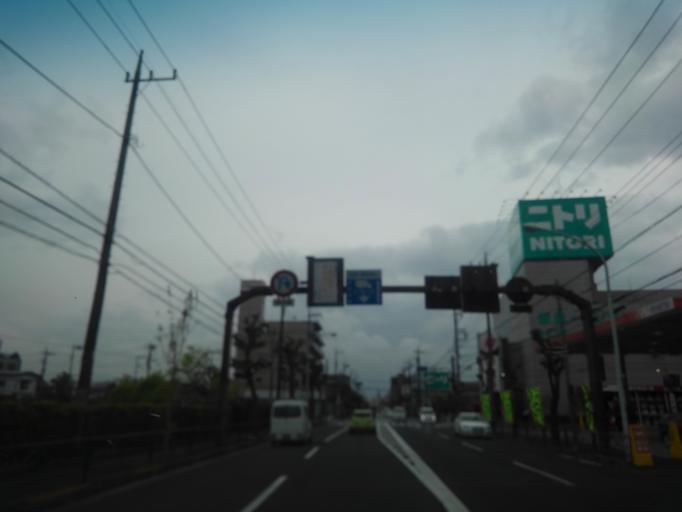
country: JP
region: Tokyo
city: Tanashicho
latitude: 35.7346
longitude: 139.5280
